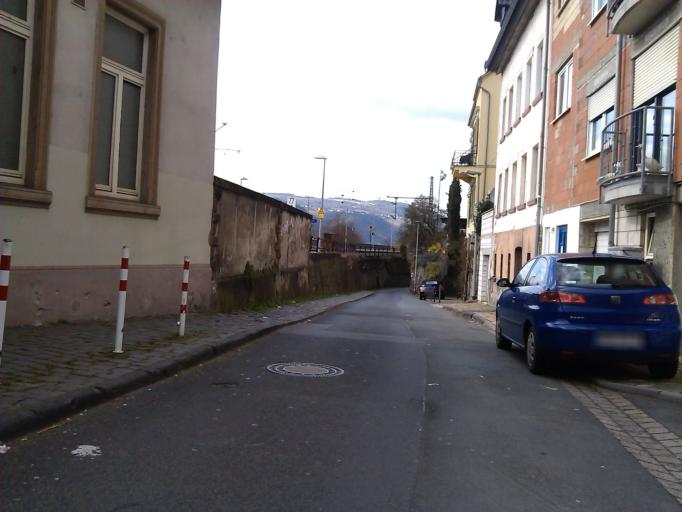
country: DE
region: Rheinland-Pfalz
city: Niederheimbach
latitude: 50.0405
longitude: 7.8129
